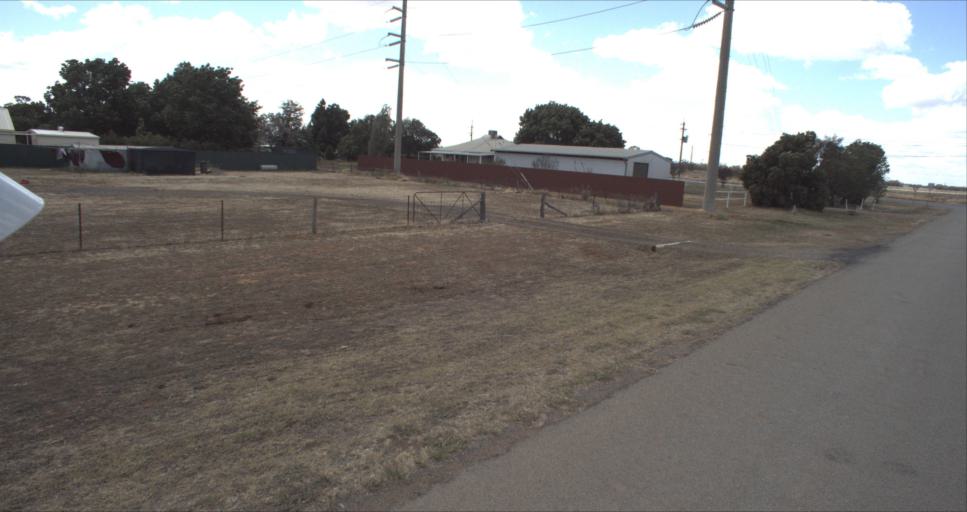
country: AU
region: New South Wales
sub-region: Murrumbidgee Shire
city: Darlington Point
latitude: -34.5122
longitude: 146.1849
